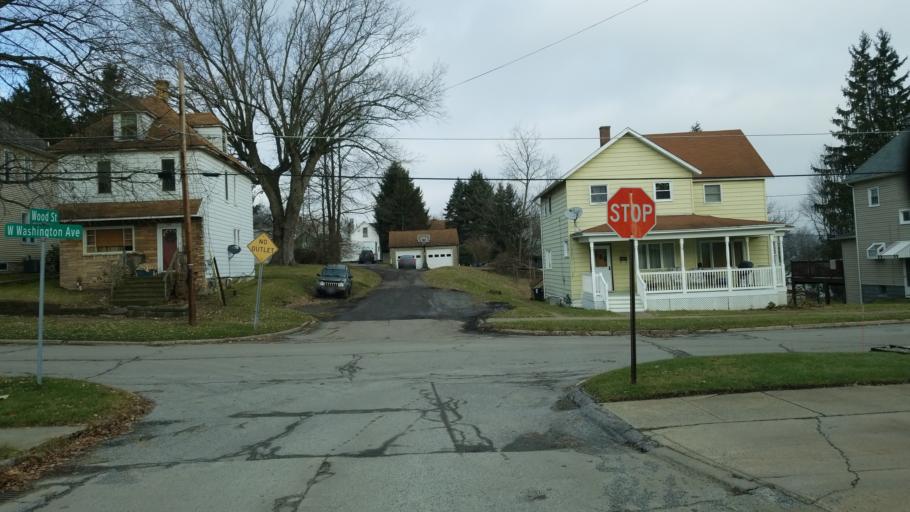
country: US
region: Pennsylvania
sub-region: Clearfield County
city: DuBois
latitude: 41.1220
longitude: -78.7725
